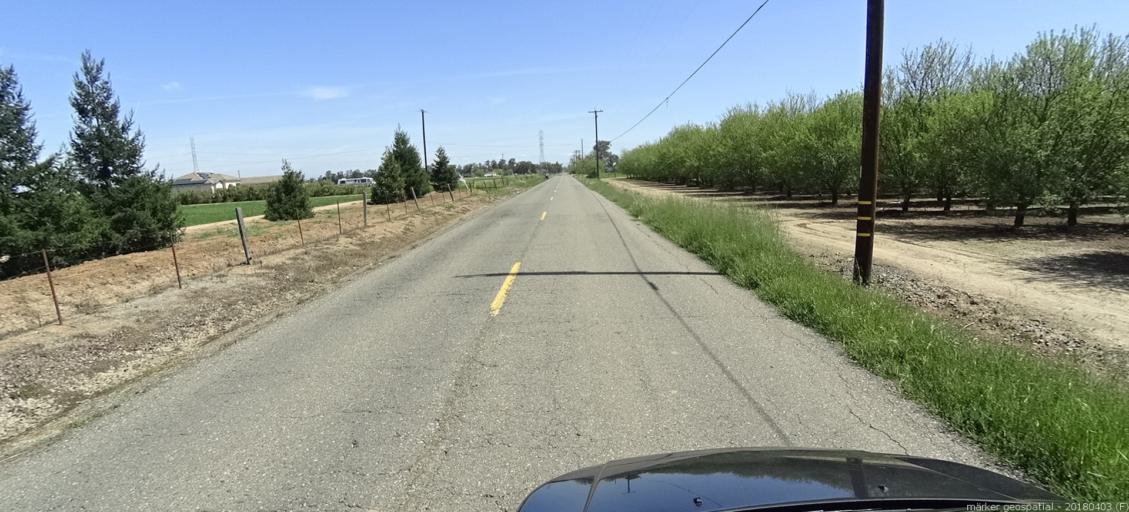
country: US
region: California
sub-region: Sacramento County
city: Wilton
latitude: 38.3799
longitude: -121.2854
